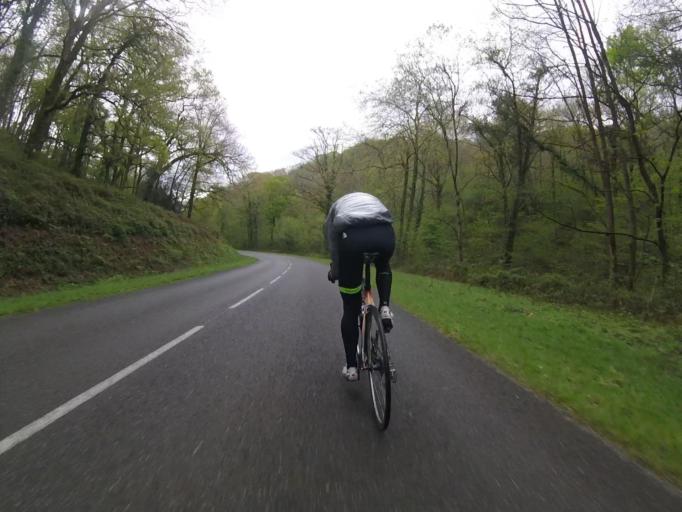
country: FR
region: Aquitaine
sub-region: Departement des Pyrenees-Atlantiques
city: Sare
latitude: 43.2838
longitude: -1.6161
